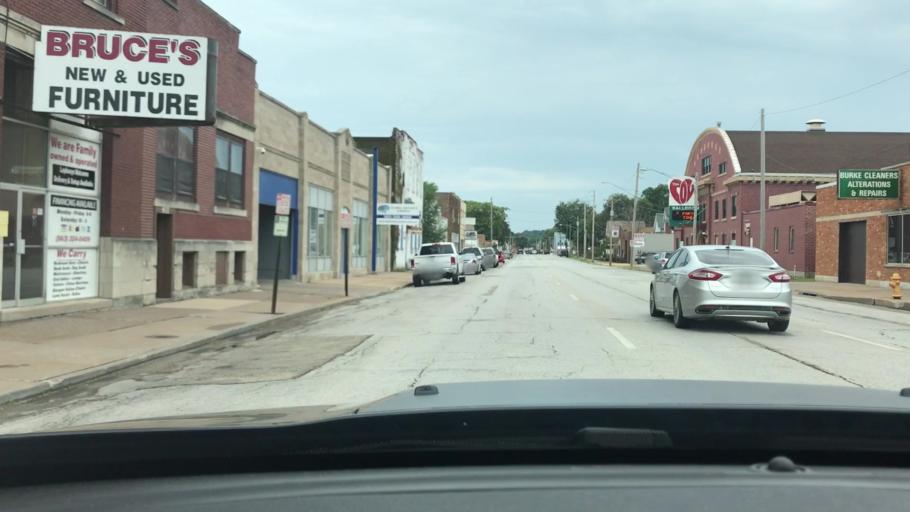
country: US
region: Iowa
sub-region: Scott County
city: Davenport
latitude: 41.5235
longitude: -90.5872
